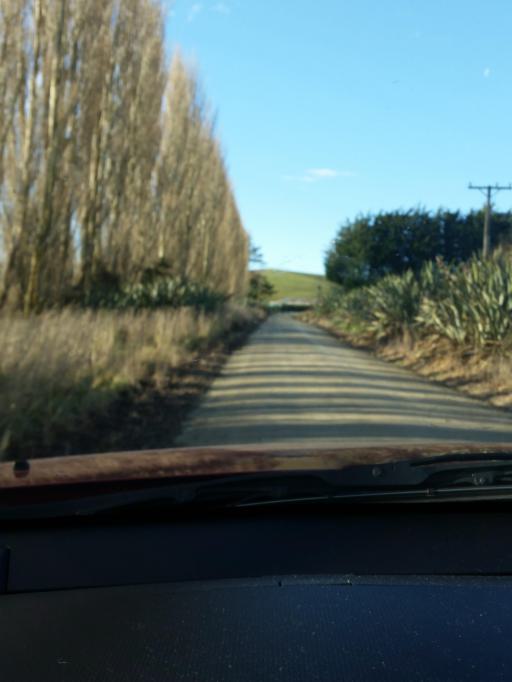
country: NZ
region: Southland
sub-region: Gore District
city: Gore
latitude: -46.2066
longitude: 168.7703
